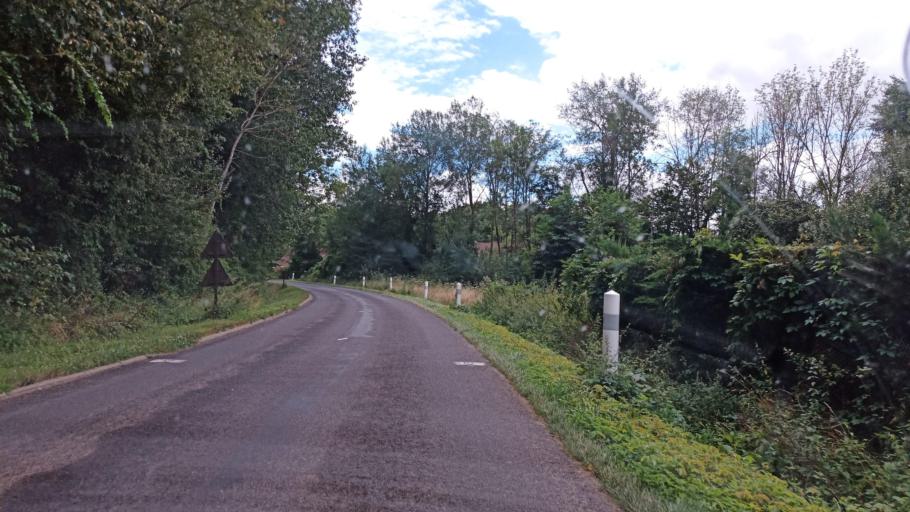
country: FR
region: Ile-de-France
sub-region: Departement de Seine-et-Marne
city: Voulx
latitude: 48.2555
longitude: 3.0180
